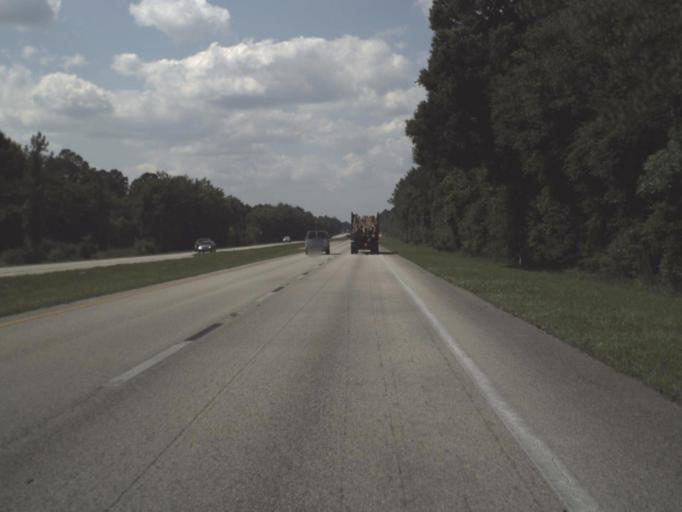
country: US
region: Florida
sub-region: Alachua County
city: Hawthorne
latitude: 29.6514
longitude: -82.1109
